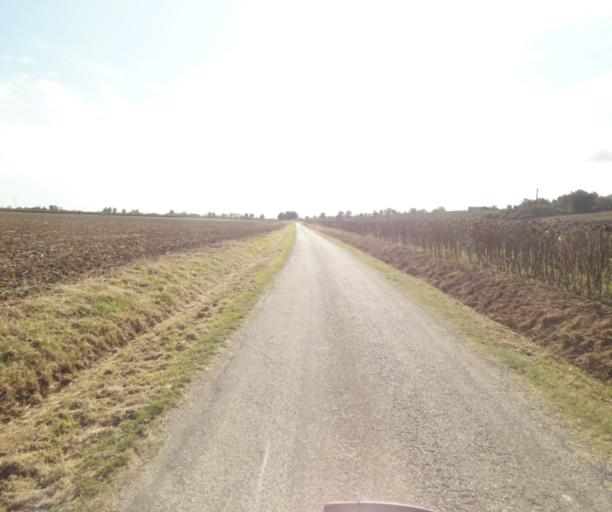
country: FR
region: Midi-Pyrenees
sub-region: Departement du Tarn-et-Garonne
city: Verdun-sur-Garonne
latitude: 43.8536
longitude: 1.1939
